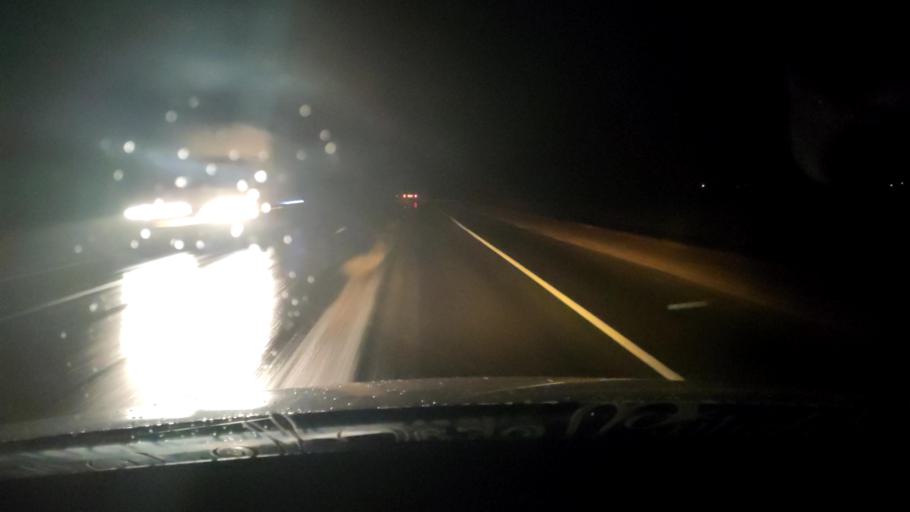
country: RU
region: Voronezj
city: Latnaya
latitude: 51.6393
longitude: 38.8968
